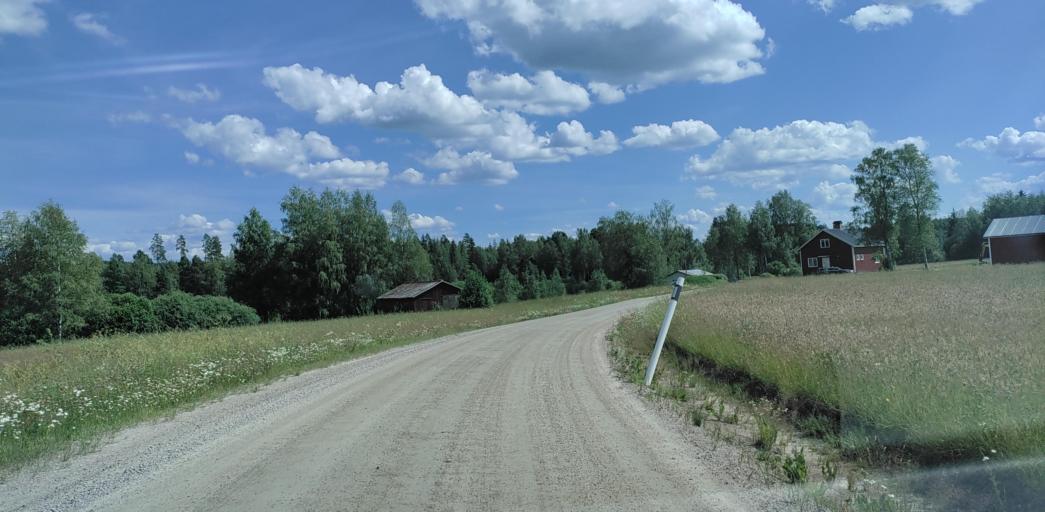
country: SE
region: Vaermland
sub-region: Hagfors Kommun
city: Ekshaerad
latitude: 60.1295
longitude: 13.4677
